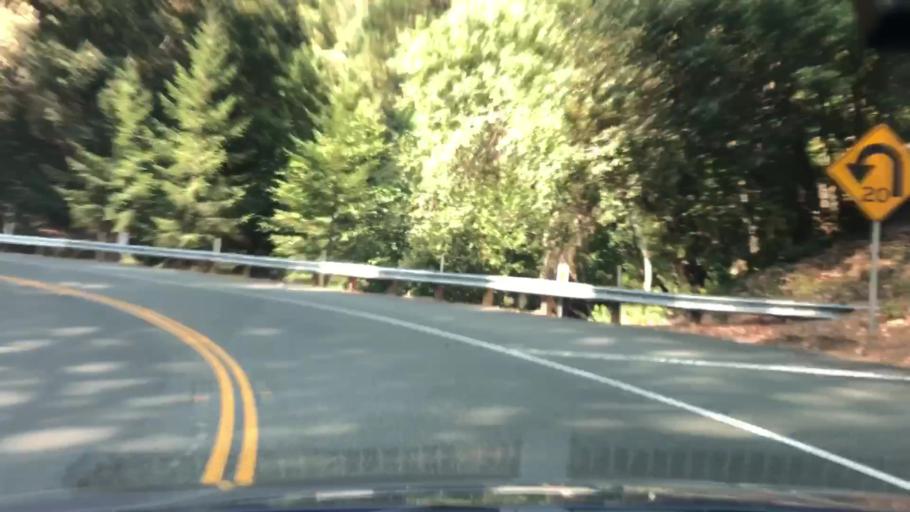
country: US
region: California
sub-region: Napa County
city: Calistoga
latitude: 38.6618
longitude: -122.5992
